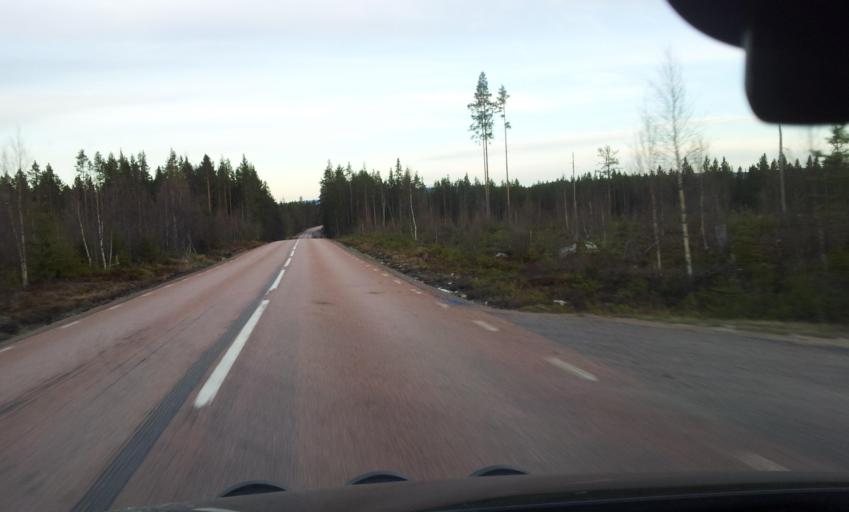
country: SE
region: Gaevleborg
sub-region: Ljusdals Kommun
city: Farila
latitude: 61.9589
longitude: 15.8785
